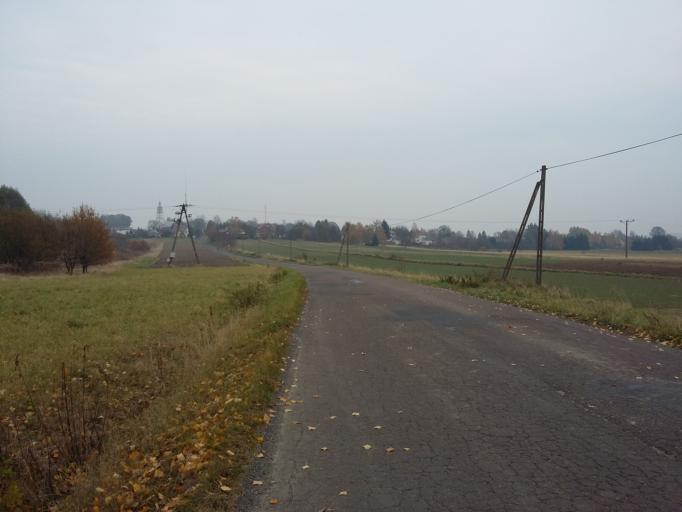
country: PL
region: Subcarpathian Voivodeship
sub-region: Powiat jasielski
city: Tarnowiec
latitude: 49.7302
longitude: 21.5673
